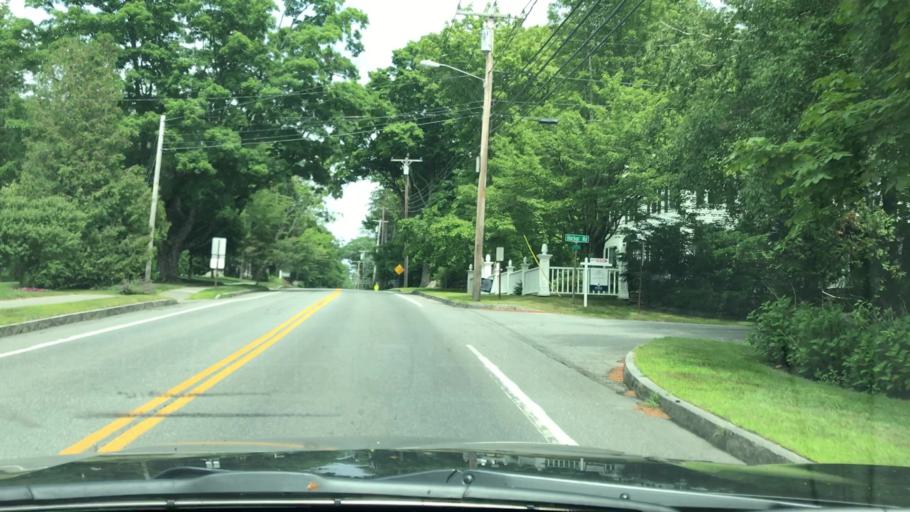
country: US
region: Maine
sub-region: Knox County
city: Camden
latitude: 44.2154
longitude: -69.0599
